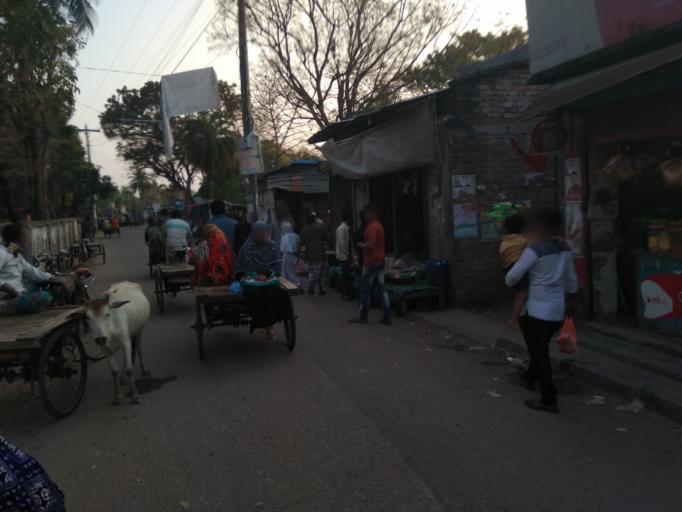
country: BD
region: Khulna
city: Satkhira
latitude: 22.5473
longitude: 89.1750
